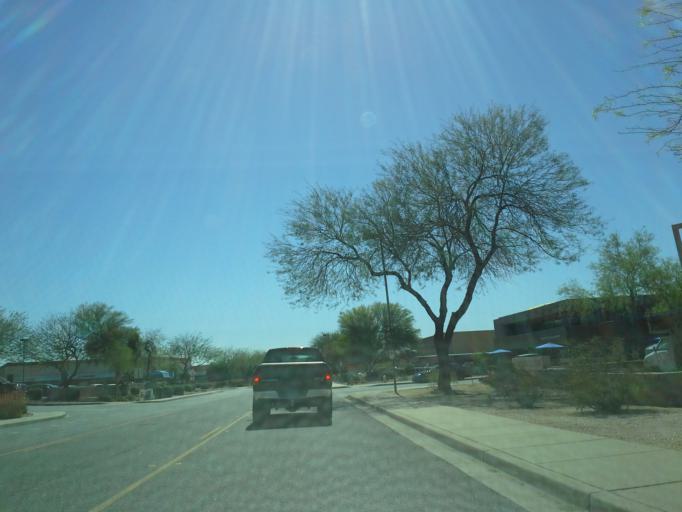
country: US
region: Arizona
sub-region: Maricopa County
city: Paradise Valley
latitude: 33.6228
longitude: -111.9023
